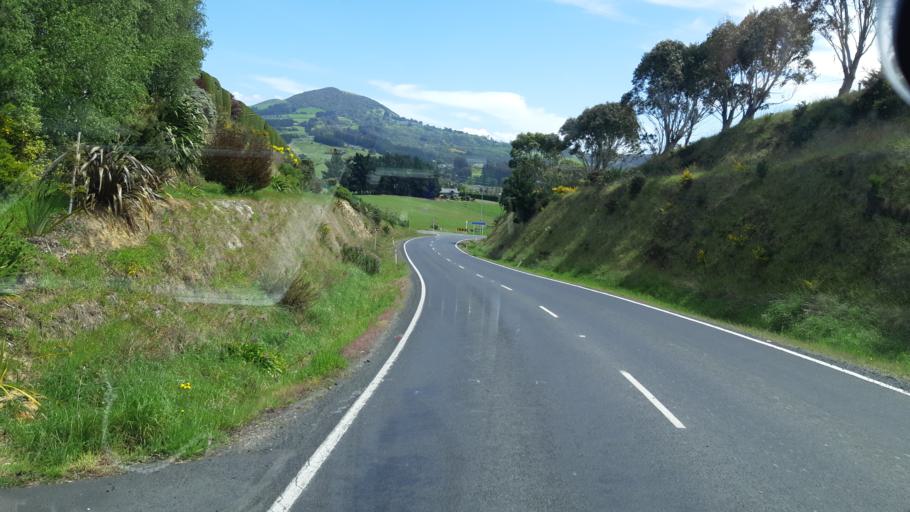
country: NZ
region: Otago
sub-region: Dunedin City
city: Dunedin
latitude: -45.9202
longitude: 170.4150
